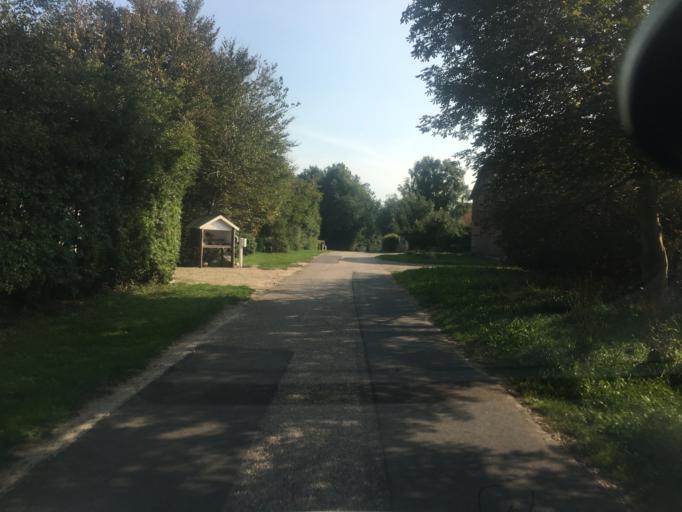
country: DK
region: South Denmark
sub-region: Tonder Kommune
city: Logumkloster
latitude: 54.9983
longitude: 8.9242
